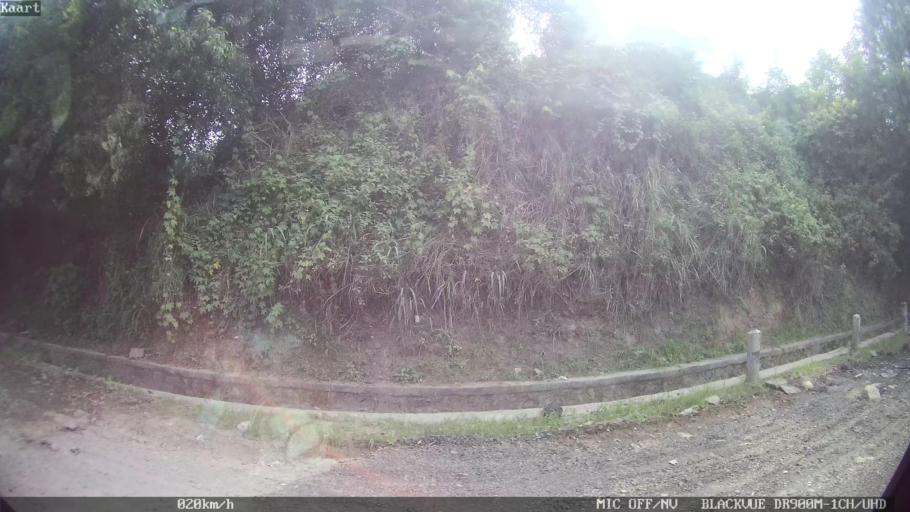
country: ID
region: Lampung
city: Panjang
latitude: -5.4405
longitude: 105.3067
